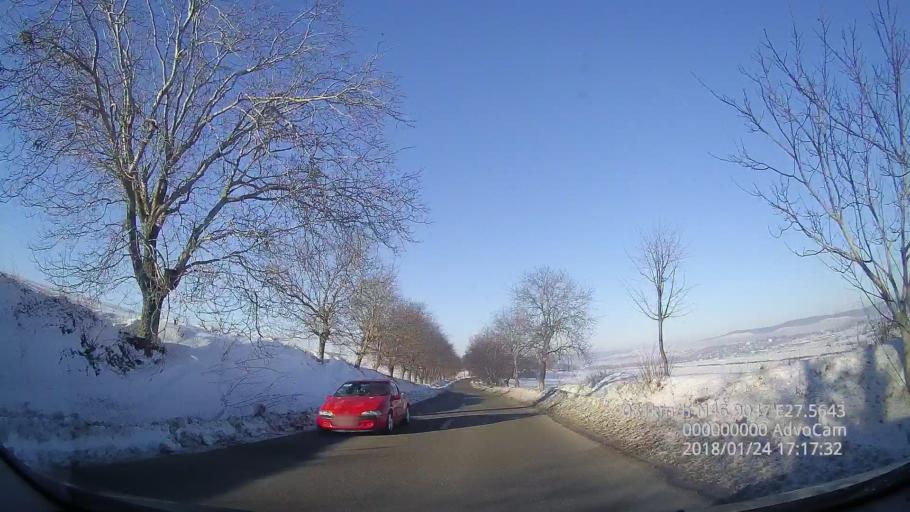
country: RO
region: Iasi
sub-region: Comuna Scanteia
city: Scanteia
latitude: 46.9054
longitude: 27.5643
